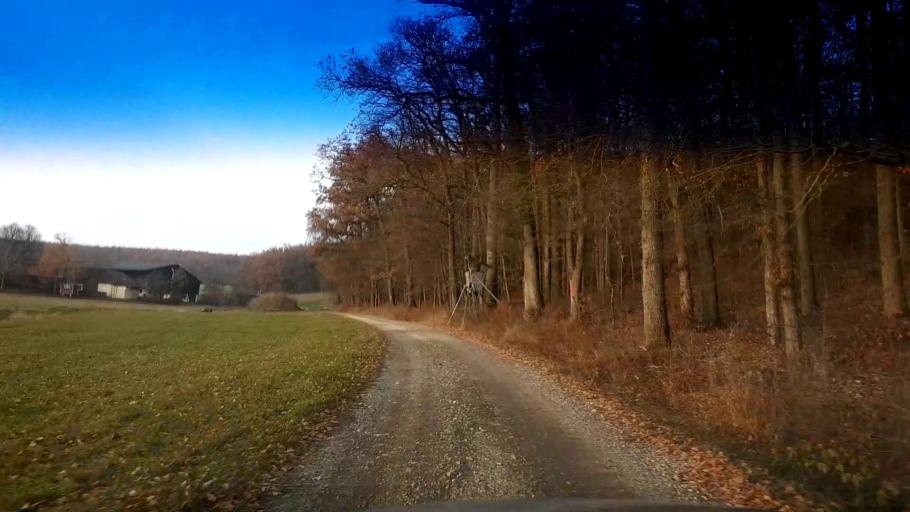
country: DE
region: Bavaria
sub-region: Upper Franconia
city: Schesslitz
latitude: 49.9853
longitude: 10.9852
